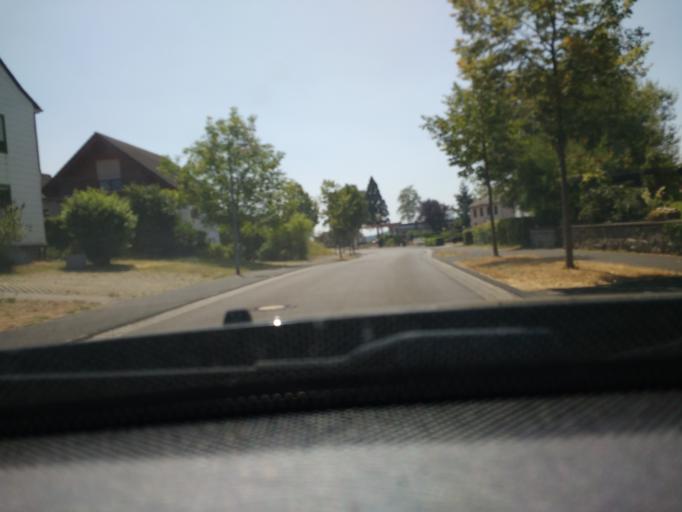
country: DE
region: Rheinland-Pfalz
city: Manderscheid
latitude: 50.0904
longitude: 6.8072
